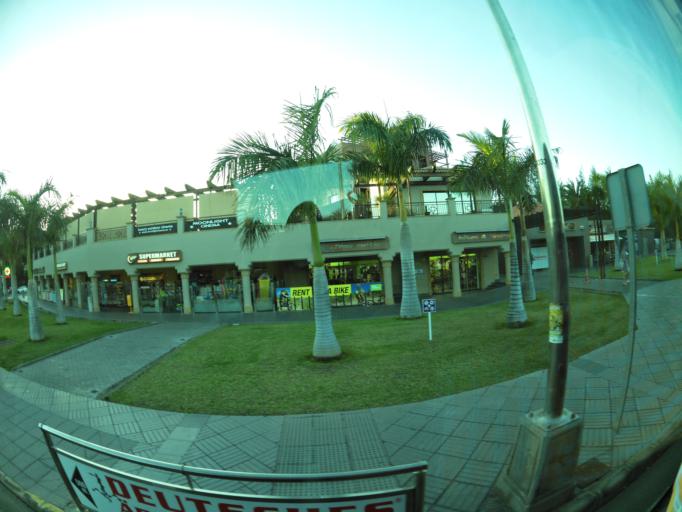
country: ES
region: Canary Islands
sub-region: Provincia de Las Palmas
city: Maspalomas
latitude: 27.7392
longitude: -15.5983
